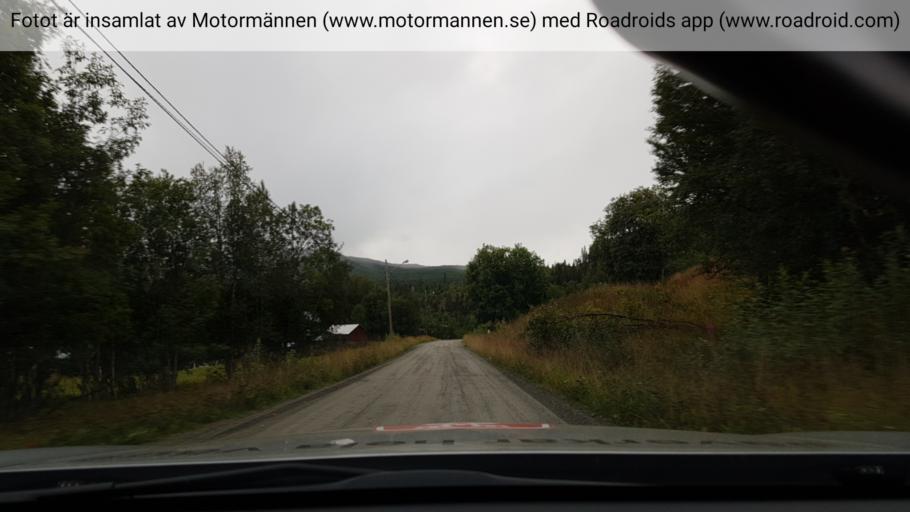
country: NO
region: Nordland
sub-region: Hattfjelldal
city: Hattfjelldal
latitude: 65.6600
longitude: 15.1301
